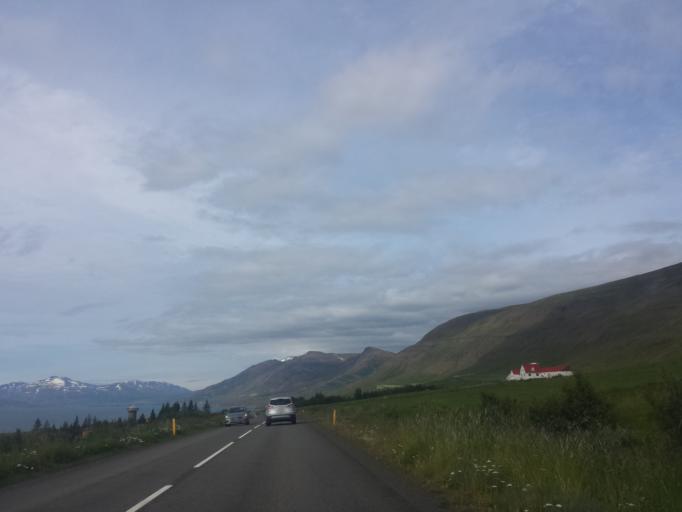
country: IS
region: Northeast
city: Akureyri
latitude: 65.7692
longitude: -18.0710
